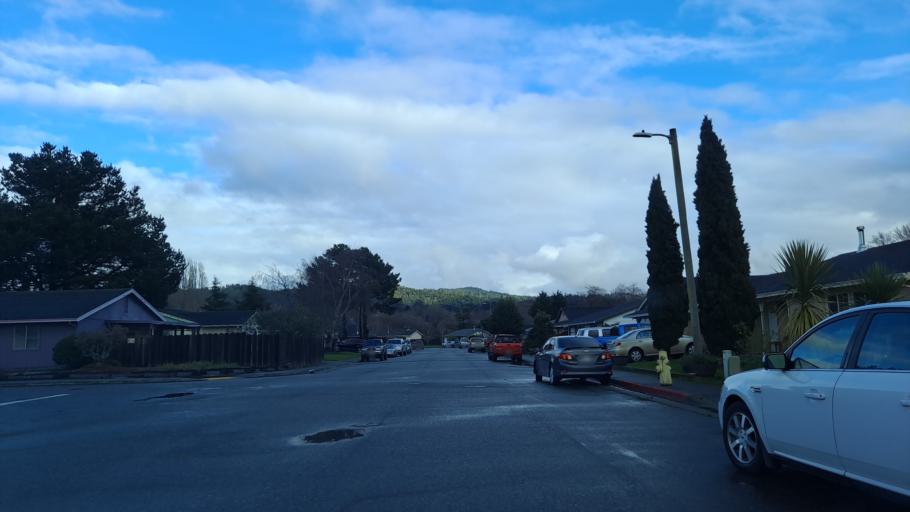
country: US
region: California
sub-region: Humboldt County
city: Fortuna
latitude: 40.5825
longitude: -124.1432
